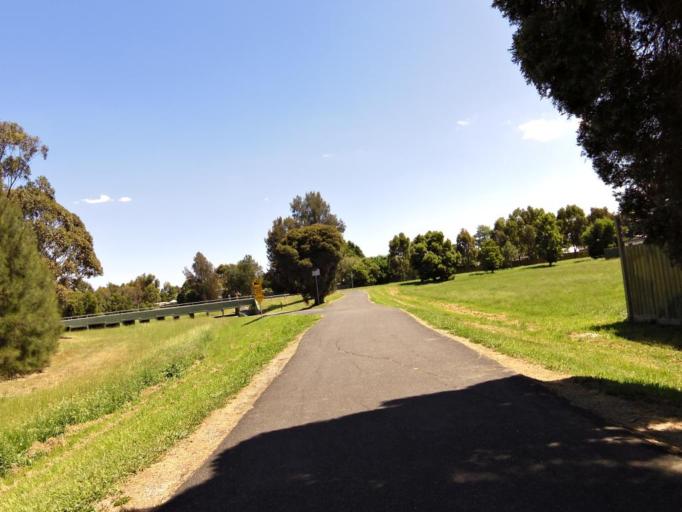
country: AU
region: Victoria
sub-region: Knox
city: Knoxfield
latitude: -37.8926
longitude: 145.2714
